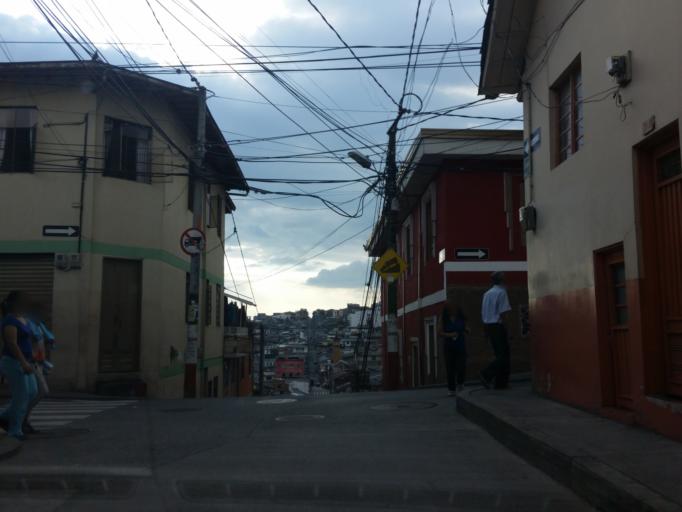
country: CO
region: Caldas
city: Manizales
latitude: 5.0655
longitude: -75.5122
